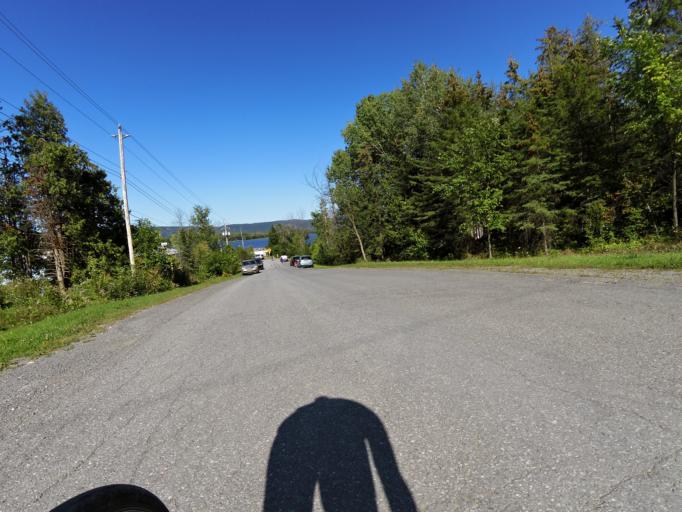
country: CA
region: Ontario
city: Bells Corners
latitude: 45.4757
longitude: -75.9947
